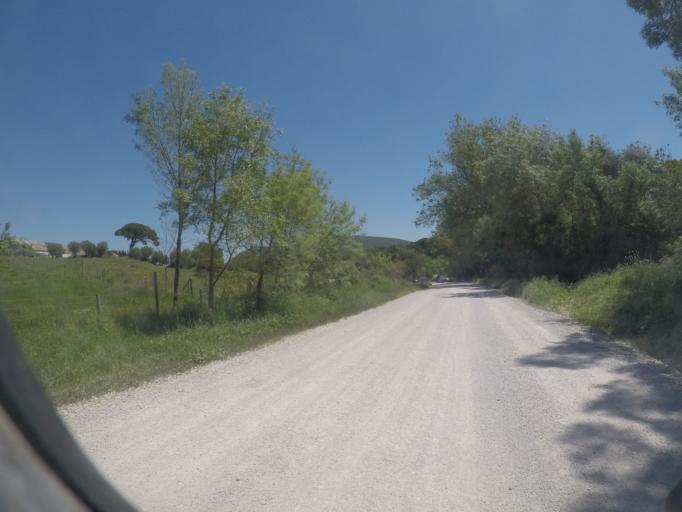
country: PT
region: Setubal
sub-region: Sesimbra
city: Sesimbra
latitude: 38.4615
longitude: -9.0576
